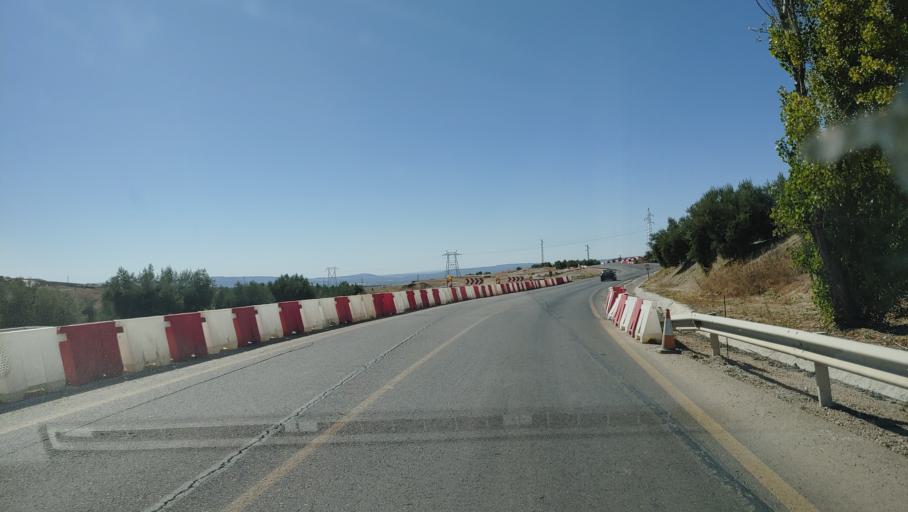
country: ES
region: Andalusia
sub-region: Provincia de Jaen
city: Iznatoraf
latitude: 38.1403
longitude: -3.0394
